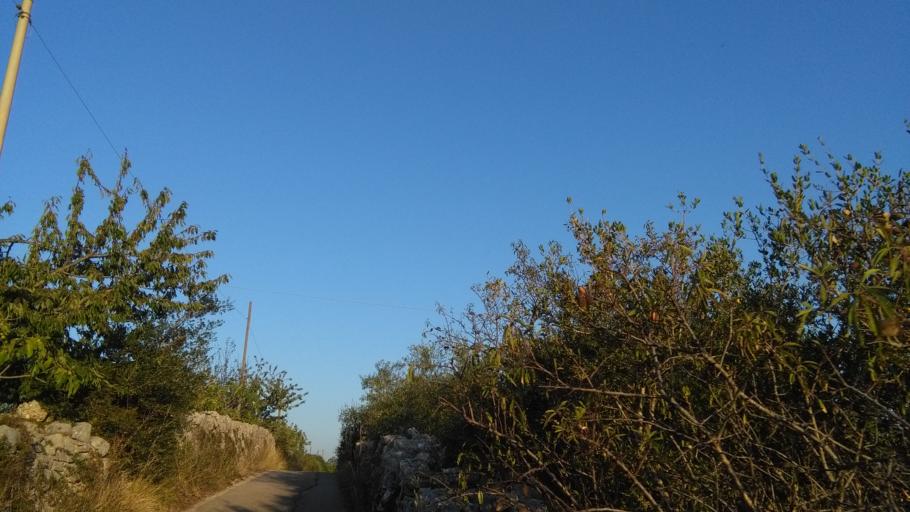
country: IT
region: Apulia
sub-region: Provincia di Bari
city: Putignano
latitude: 40.8234
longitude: 17.1011
